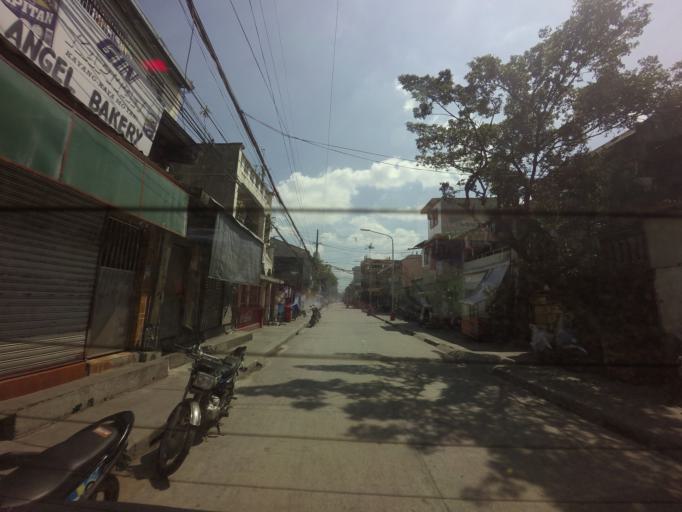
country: PH
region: Metro Manila
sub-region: Caloocan City
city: Niugan
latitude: 14.6486
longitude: 120.9578
